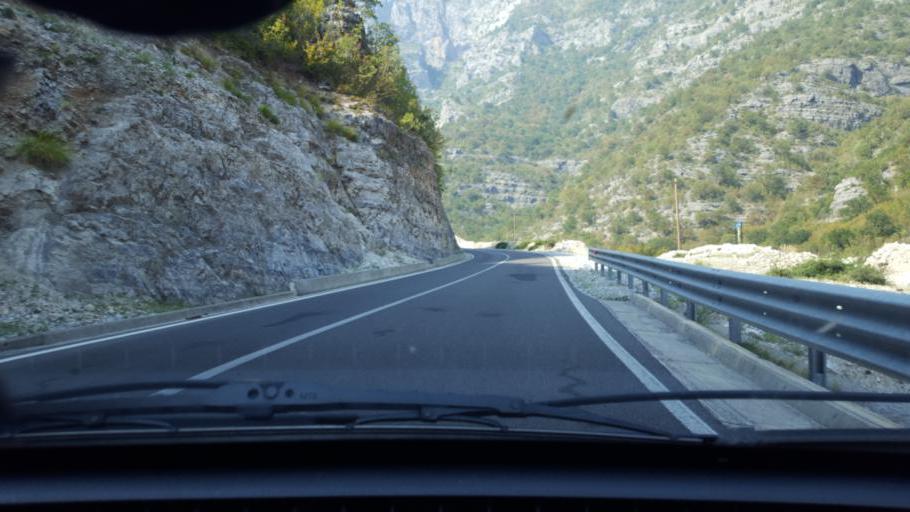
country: AL
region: Shkoder
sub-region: Rrethi i Malesia e Madhe
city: Kastrat
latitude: 42.4268
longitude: 19.5227
